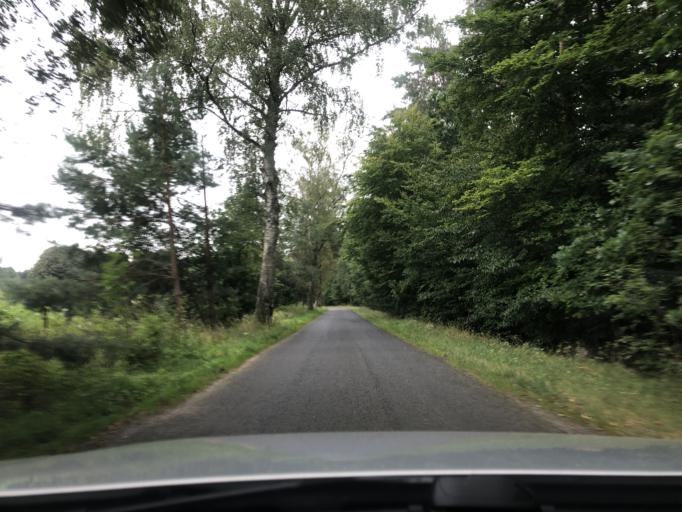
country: PL
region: Greater Poland Voivodeship
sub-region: Powiat pilski
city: Szydlowo
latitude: 53.2686
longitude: 16.6315
